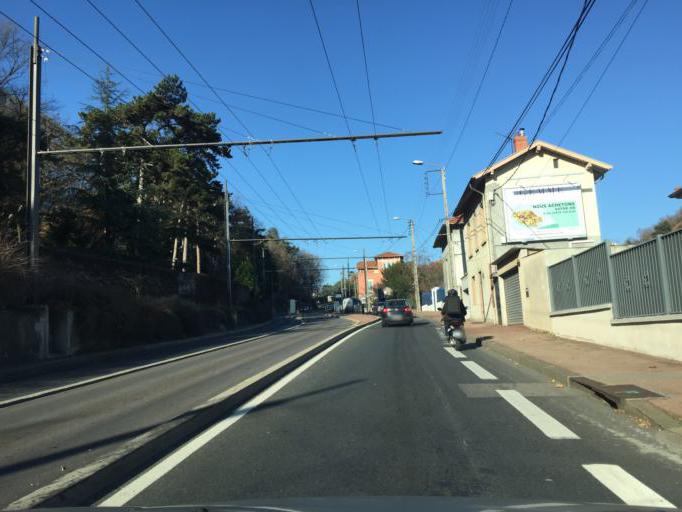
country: FR
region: Rhone-Alpes
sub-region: Departement du Rhone
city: Caluire-et-Cuire
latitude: 45.7946
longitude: 4.8593
